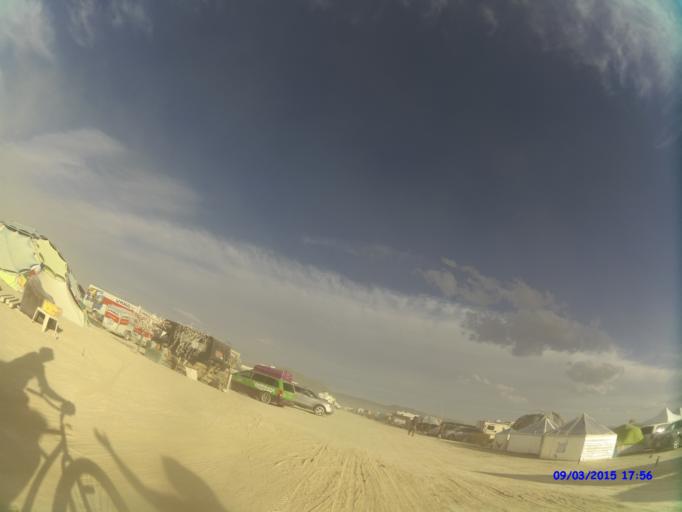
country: US
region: Nevada
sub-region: Pershing County
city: Lovelock
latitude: 40.7770
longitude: -119.2177
